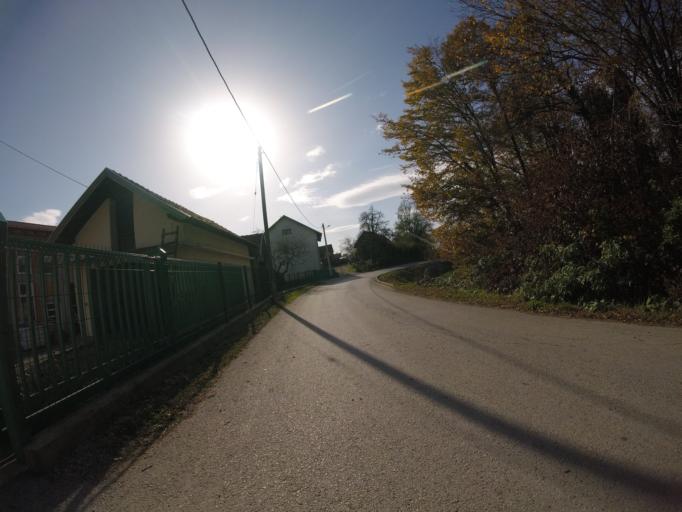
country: HR
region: Zagrebacka
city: Lukavec
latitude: 45.6149
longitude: 16.0082
